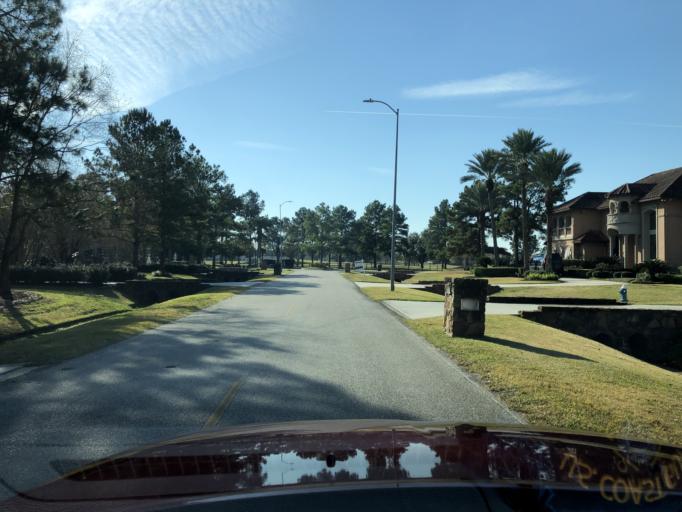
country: US
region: Texas
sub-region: Harris County
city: Tomball
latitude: 30.0382
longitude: -95.5592
